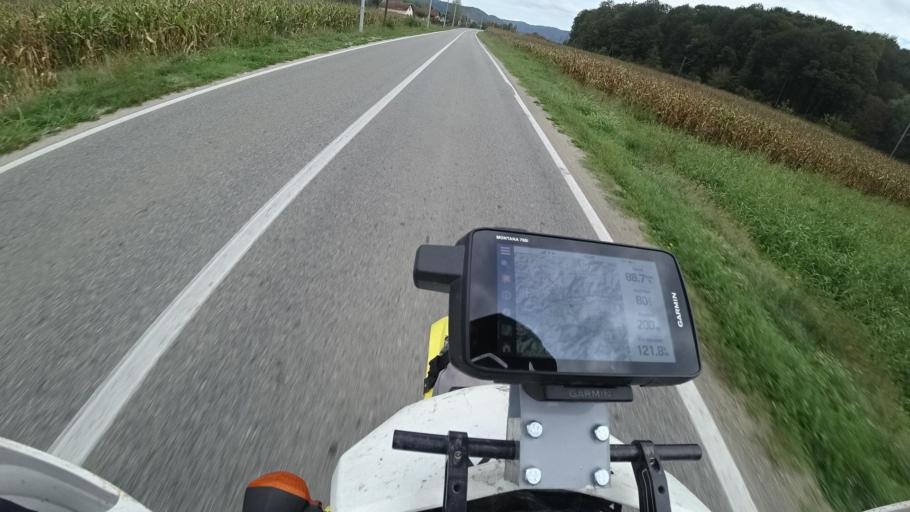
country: BA
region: Republika Srpska
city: Bosanski Novi
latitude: 44.9960
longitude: 16.2948
